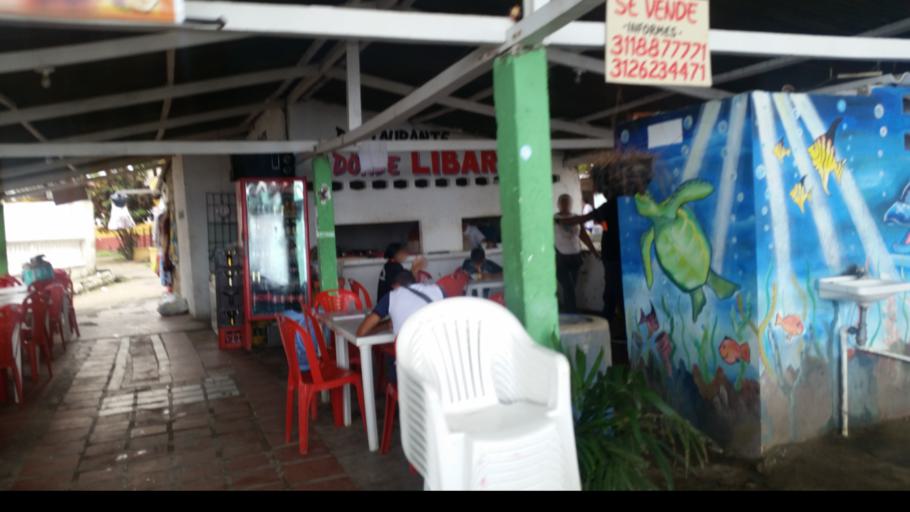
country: CO
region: Magdalena
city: Santa Marta
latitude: 11.2626
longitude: -73.7691
